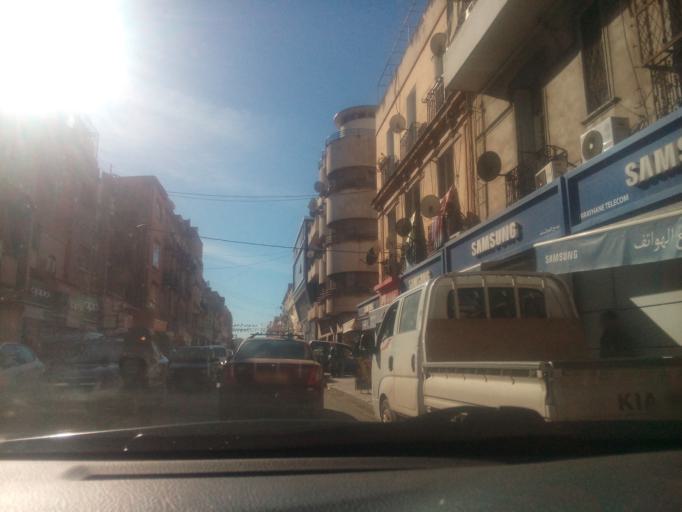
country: DZ
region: Oran
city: Oran
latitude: 35.6960
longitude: -0.6434
